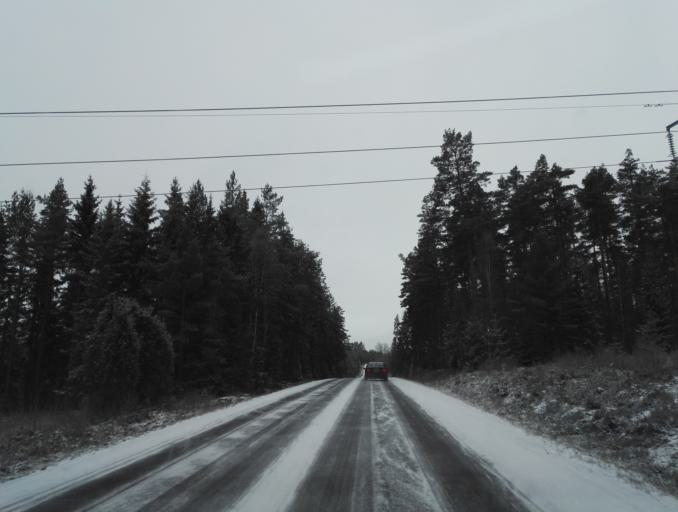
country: SE
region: Kronoberg
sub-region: Lessebo Kommun
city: Lessebo
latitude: 56.7923
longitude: 15.3148
